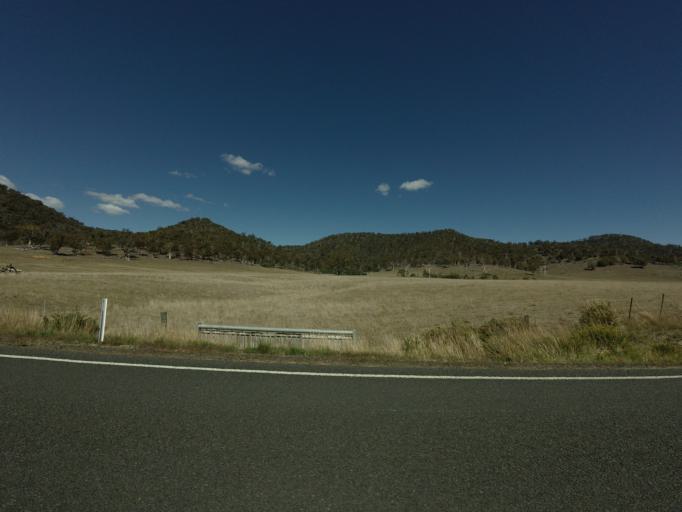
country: AU
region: Tasmania
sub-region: Break O'Day
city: St Helens
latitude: -41.6898
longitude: 147.8783
